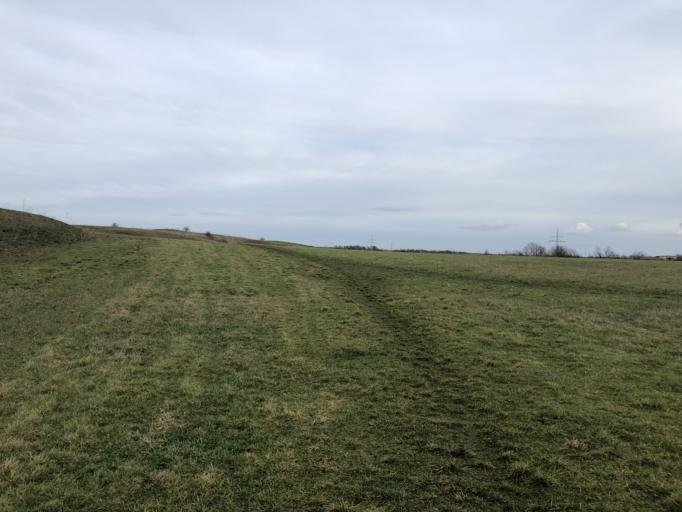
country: DE
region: Saxony-Anhalt
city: Lieskau
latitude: 51.5283
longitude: 11.8964
